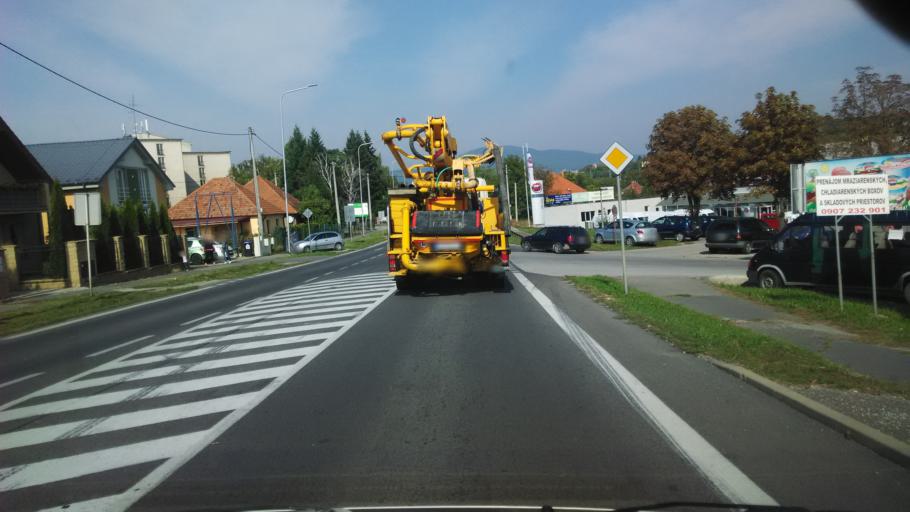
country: SK
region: Nitriansky
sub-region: Okres Nitra
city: Nitra
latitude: 48.2919
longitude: 18.0768
